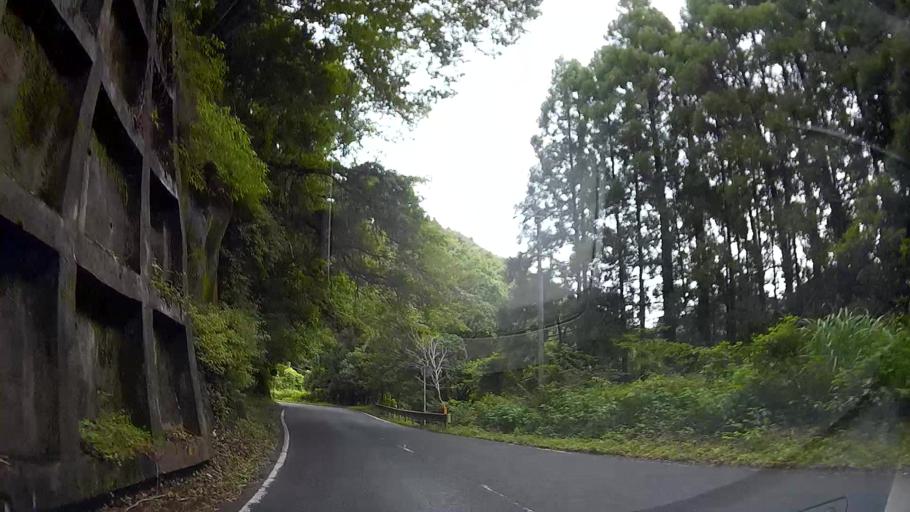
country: JP
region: Kumamoto
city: Kikuchi
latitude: 33.0959
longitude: 130.9572
